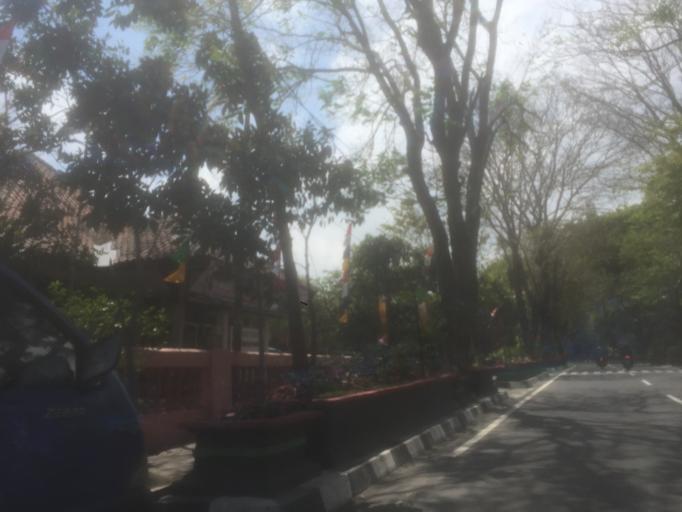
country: ID
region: Central Java
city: Muntilan
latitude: -7.5755
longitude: 110.2710
